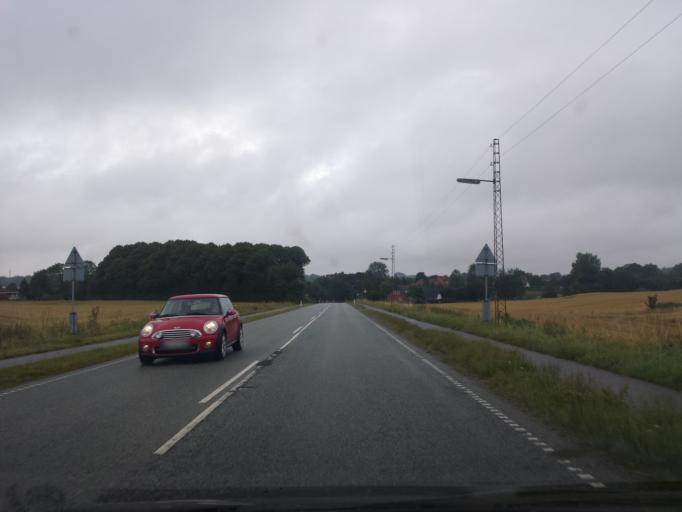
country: DK
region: South Denmark
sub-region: Sonderborg Kommune
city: Grasten
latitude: 54.9344
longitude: 9.6128
